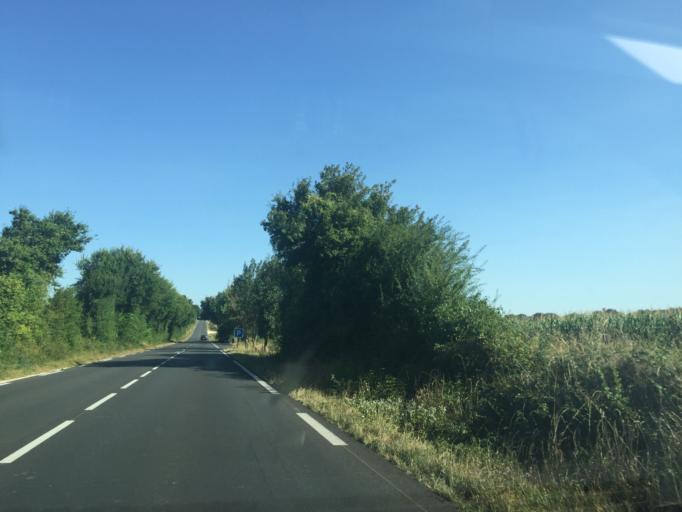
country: FR
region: Poitou-Charentes
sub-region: Departement des Deux-Sevres
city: Melle
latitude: 46.2137
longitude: -0.1160
